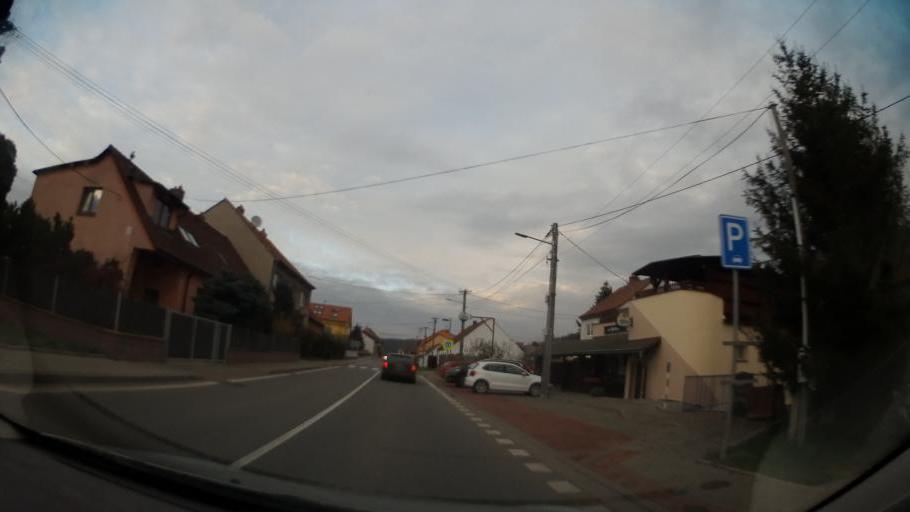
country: CZ
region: South Moravian
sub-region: Okres Brno-Venkov
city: Rosice
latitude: 49.1672
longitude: 16.4015
